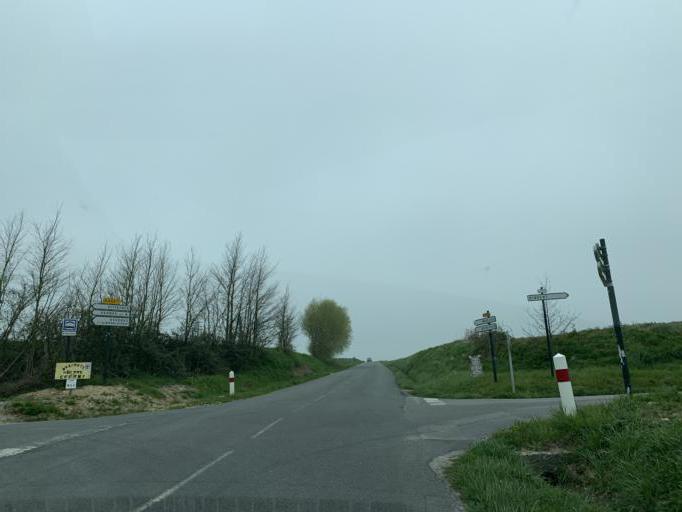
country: FR
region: Nord-Pas-de-Calais
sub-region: Departement du Pas-de-Calais
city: Rinxent
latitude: 50.7854
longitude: 1.7267
